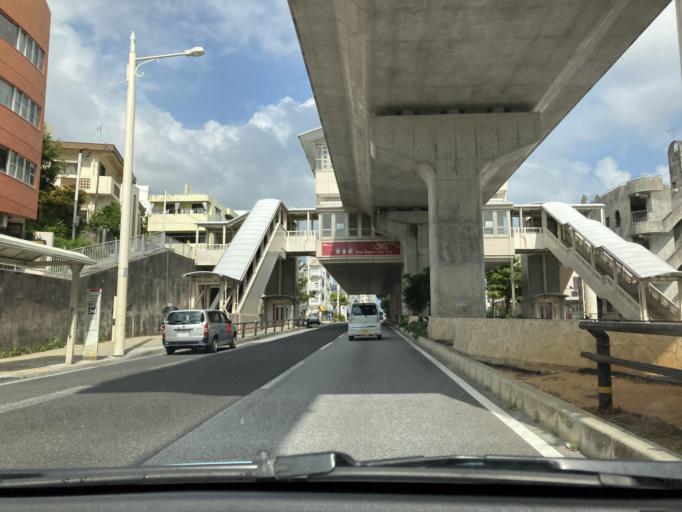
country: JP
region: Okinawa
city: Naha-shi
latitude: 26.2189
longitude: 127.7249
